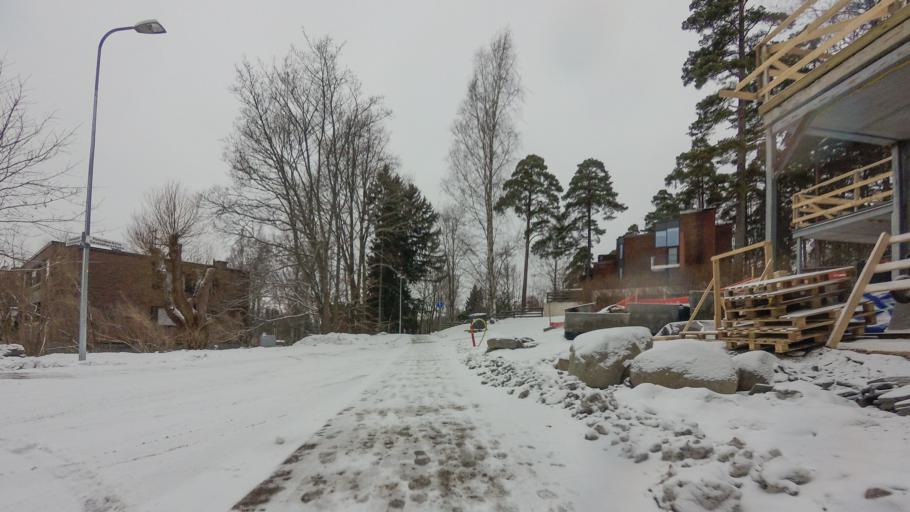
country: FI
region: Uusimaa
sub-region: Helsinki
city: Vantaa
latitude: 60.1915
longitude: 25.0641
